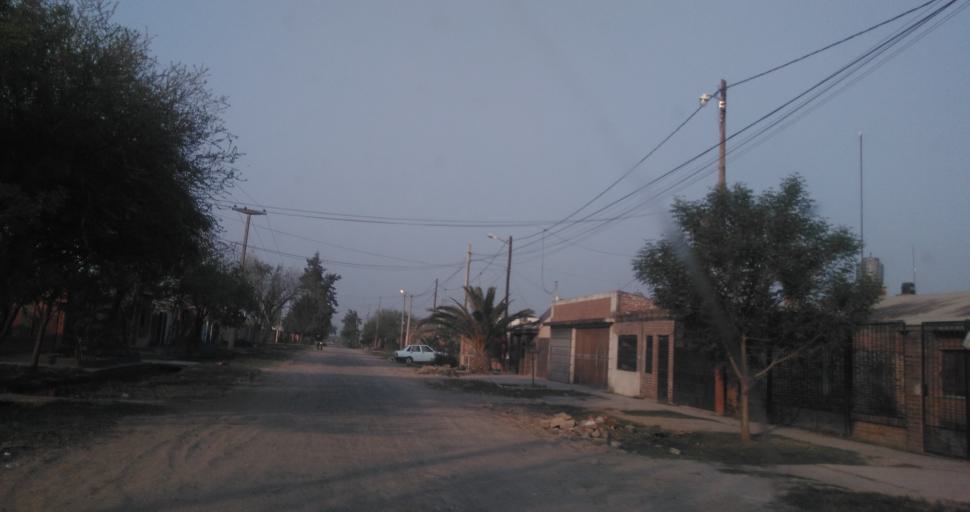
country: AR
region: Chaco
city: Resistencia
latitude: -27.4775
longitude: -59.0054
